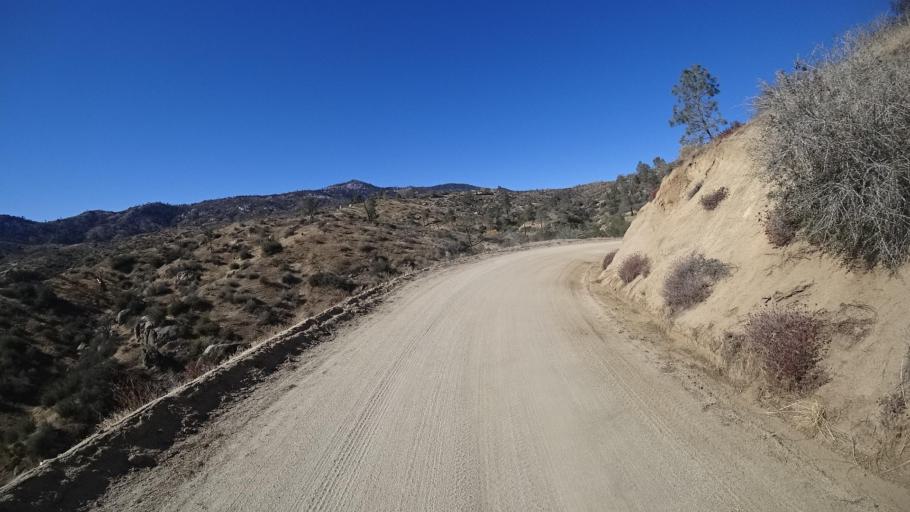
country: US
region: California
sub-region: Kern County
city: Wofford Heights
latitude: 35.7056
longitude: -118.4959
